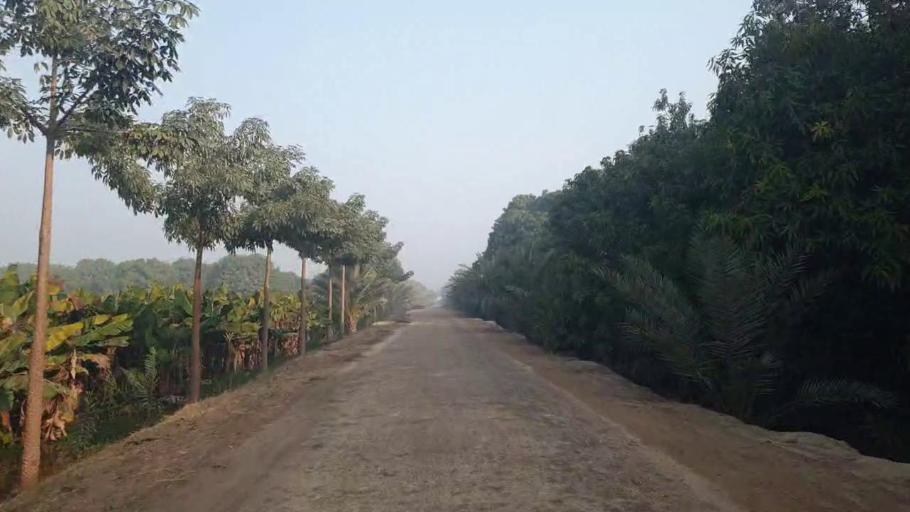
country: PK
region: Sindh
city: Tando Adam
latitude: 25.7902
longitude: 68.6403
